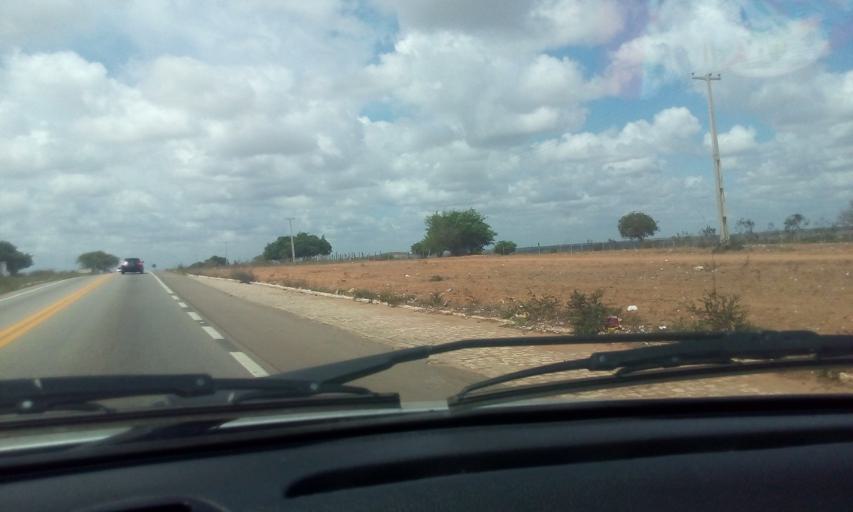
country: BR
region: Rio Grande do Norte
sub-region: Sao Paulo Do Potengi
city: Sao Paulo do Potengi
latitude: -5.9878
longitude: -35.5896
